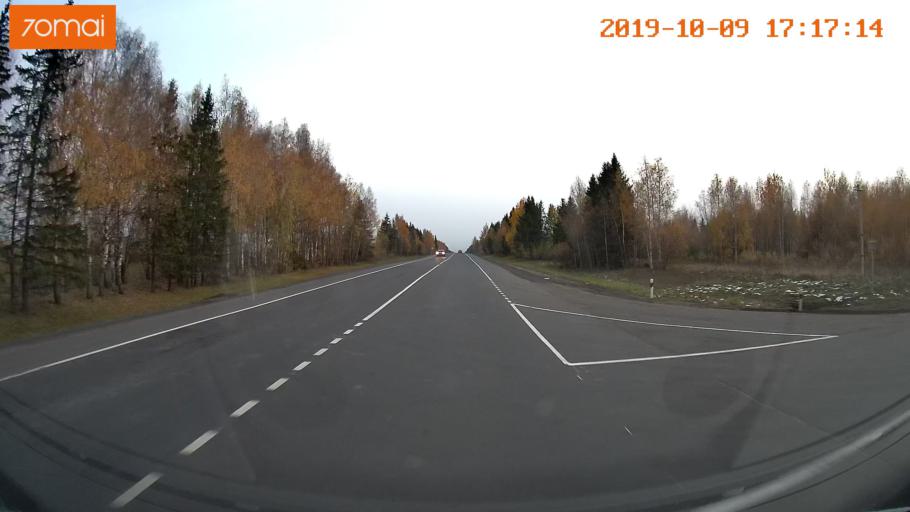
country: RU
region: Ivanovo
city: Furmanov
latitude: 57.2787
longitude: 41.1588
